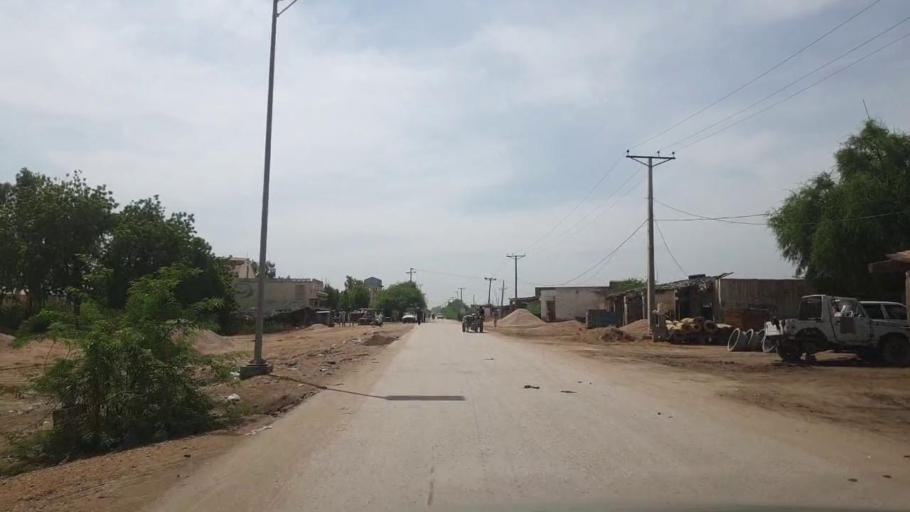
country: PK
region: Sindh
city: Kot Diji
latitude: 27.1640
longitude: 68.9542
